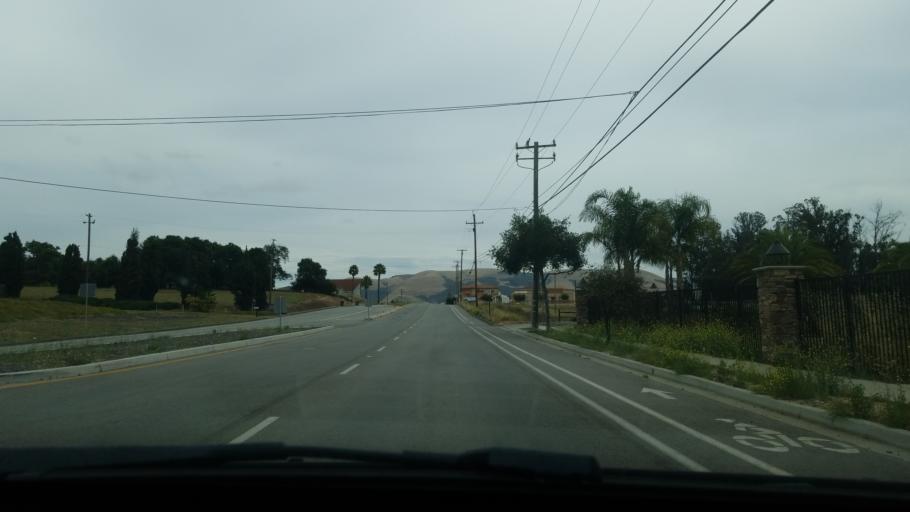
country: US
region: California
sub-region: San Luis Obispo County
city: Nipomo
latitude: 35.0326
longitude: -120.4920
